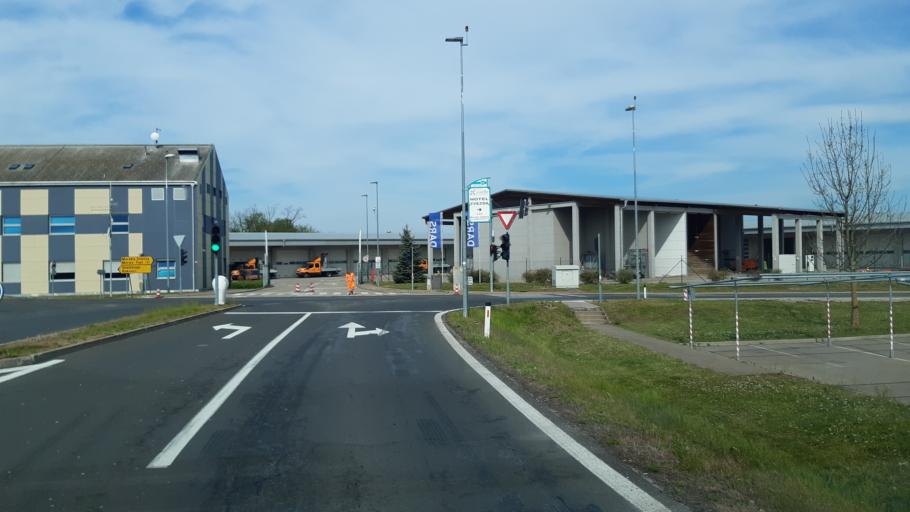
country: SI
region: Murska Sobota
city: Bakovci
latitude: 46.6327
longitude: 16.1567
